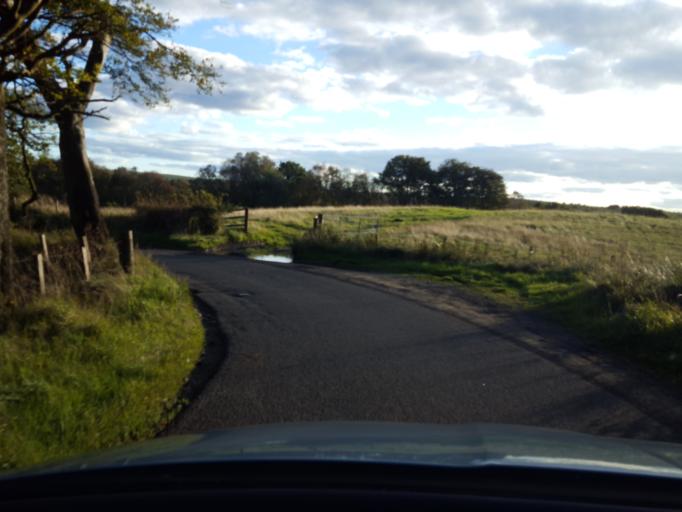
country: GB
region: Scotland
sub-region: North Lanarkshire
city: Cumbernauld
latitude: 55.9319
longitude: -3.9471
